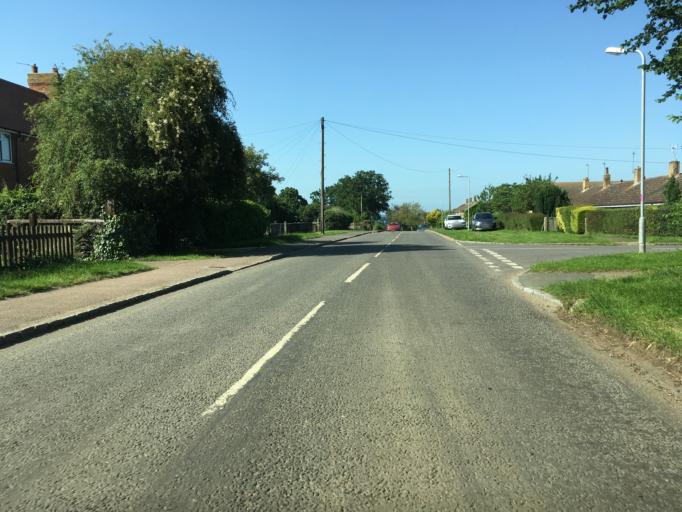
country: GB
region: England
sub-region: Buckinghamshire
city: Steeple Claydon
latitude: 51.9368
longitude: -0.9783
